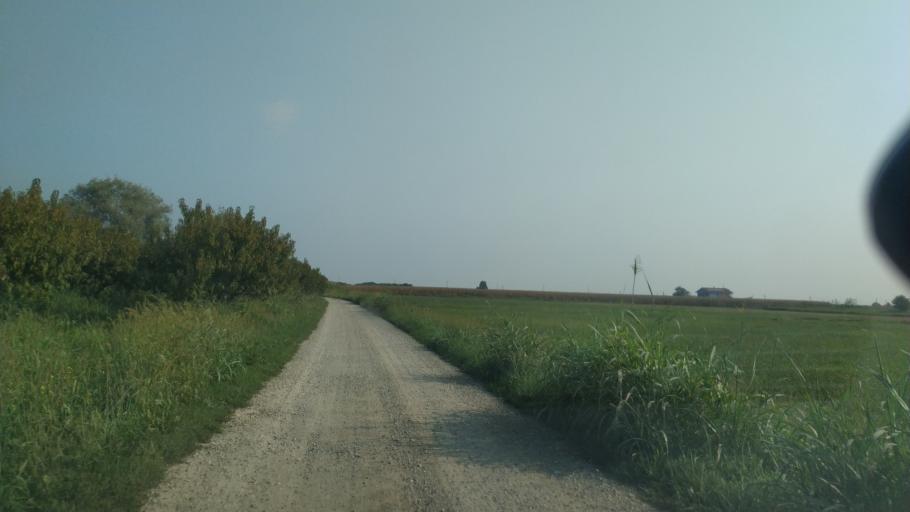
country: IT
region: Piedmont
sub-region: Provincia di Vercelli
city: Cigliano
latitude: 45.3243
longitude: 8.0308
